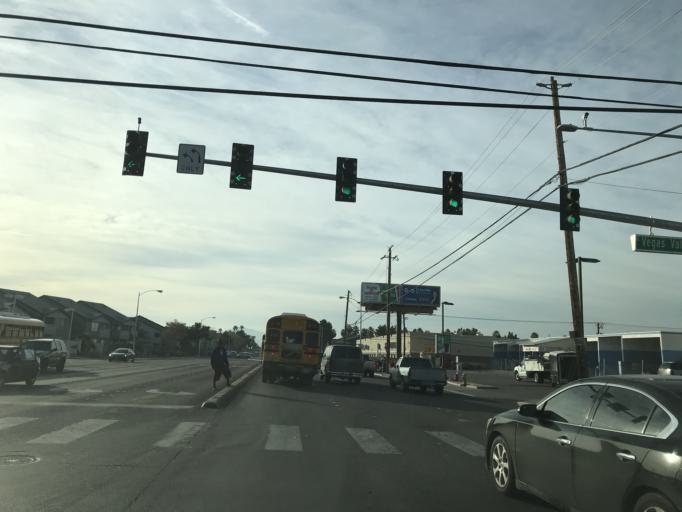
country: US
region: Nevada
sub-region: Clark County
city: Winchester
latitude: 36.1370
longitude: -115.0656
